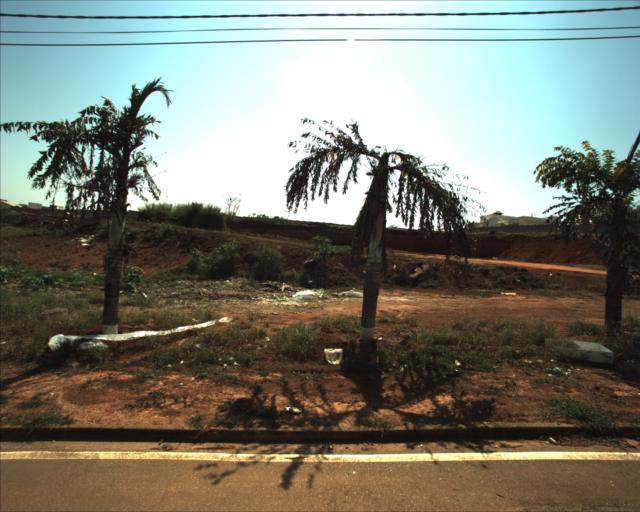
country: BR
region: Sao Paulo
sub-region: Sorocaba
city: Sorocaba
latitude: -23.4468
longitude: -47.5079
